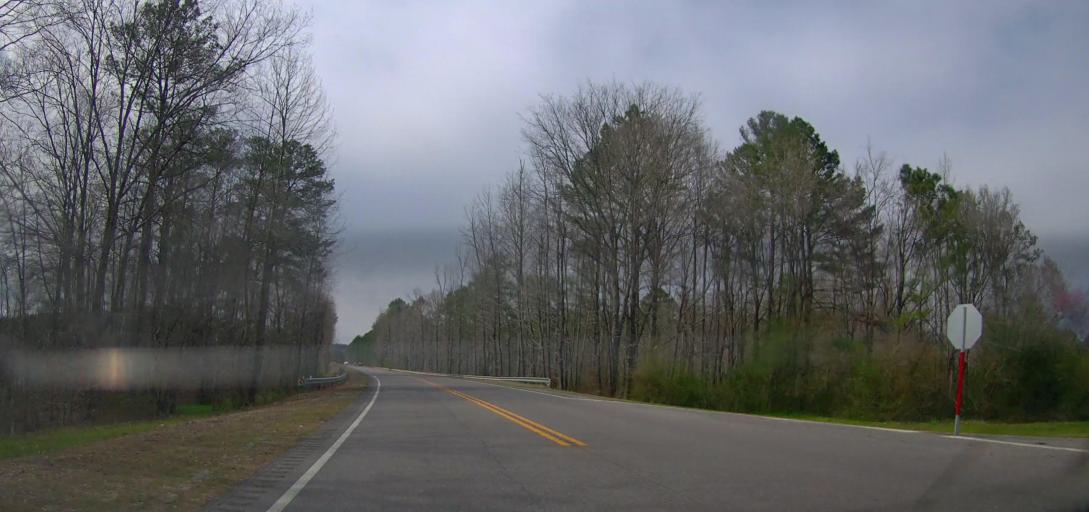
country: US
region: Alabama
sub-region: Walker County
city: Carbon Hill
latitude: 33.8975
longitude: -87.5384
